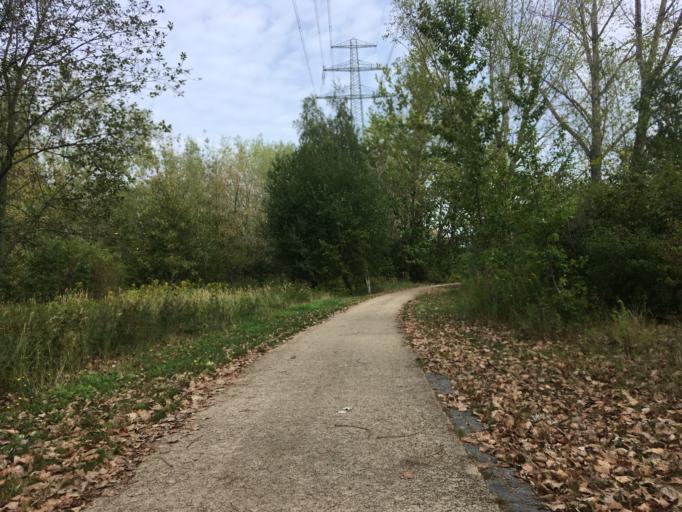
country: DE
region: Berlin
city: Falkenberg
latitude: 52.5571
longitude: 13.5430
